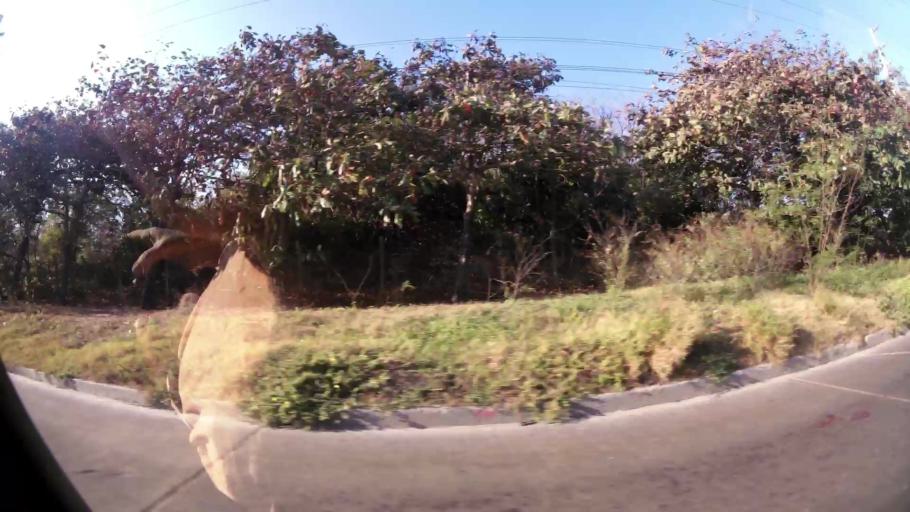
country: CO
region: Atlantico
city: Barranquilla
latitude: 11.0329
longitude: -74.8108
